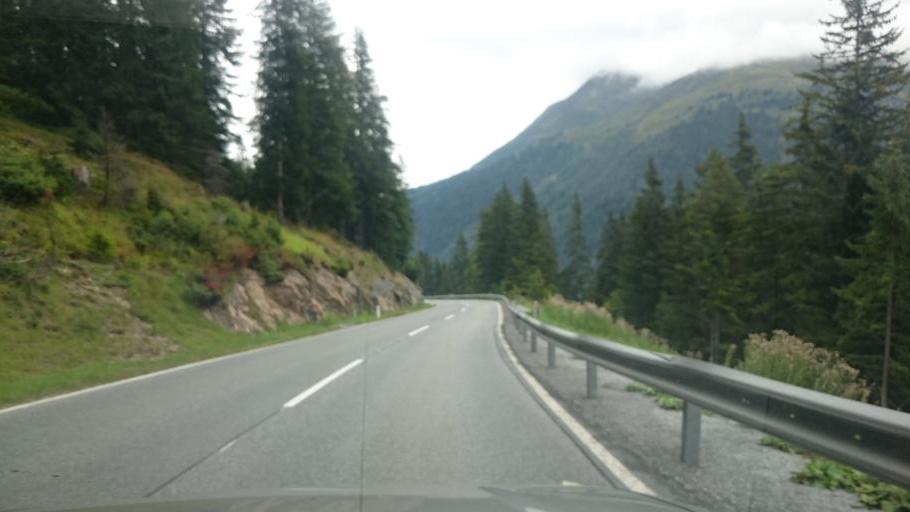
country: AT
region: Tyrol
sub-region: Politischer Bezirk Landeck
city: Sankt Anton am Arlberg
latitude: 47.1196
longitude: 10.2338
